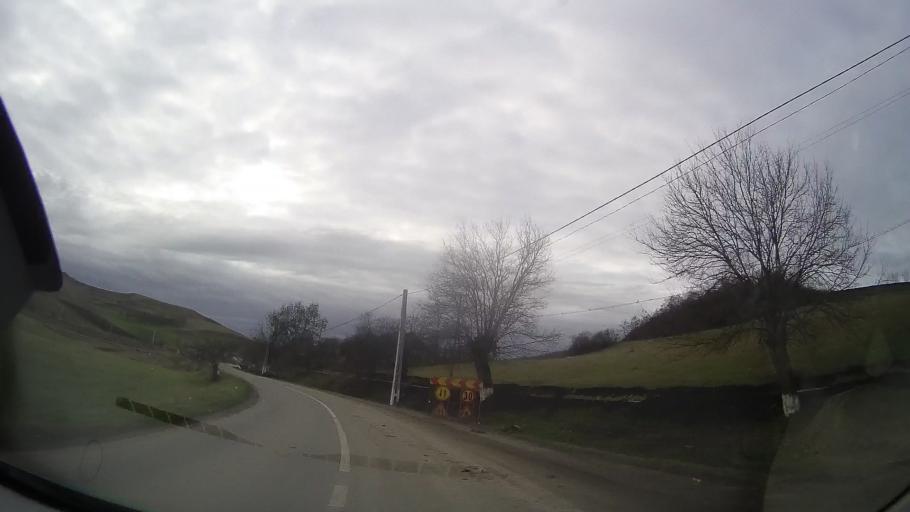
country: RO
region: Bistrita-Nasaud
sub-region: Comuna Budesti
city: Budesti
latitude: 46.8510
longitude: 24.2411
